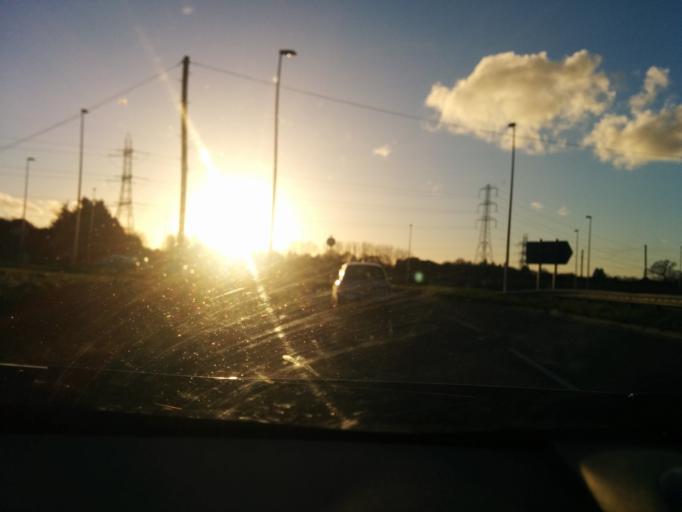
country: GB
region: England
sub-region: Buckinghamshire
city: Denham
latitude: 51.5548
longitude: -0.5032
